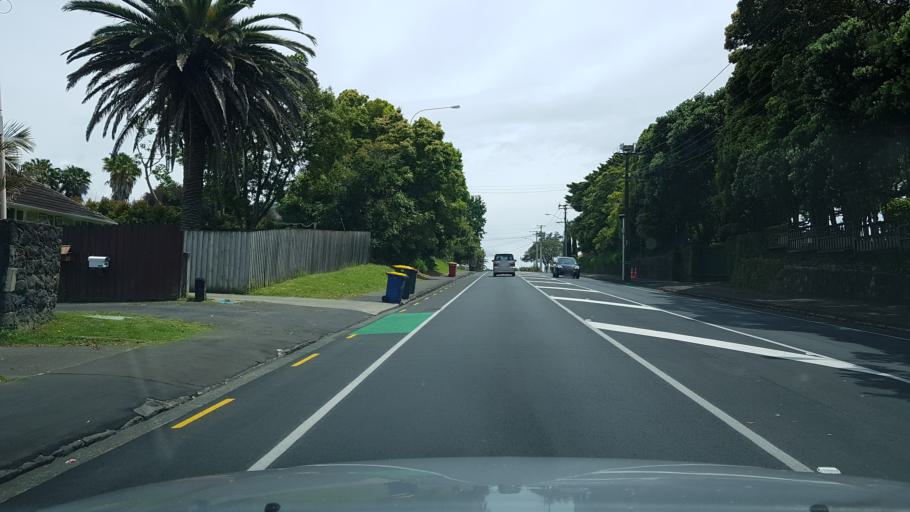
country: NZ
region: Auckland
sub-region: Auckland
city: North Shore
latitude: -36.7998
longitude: 174.7862
